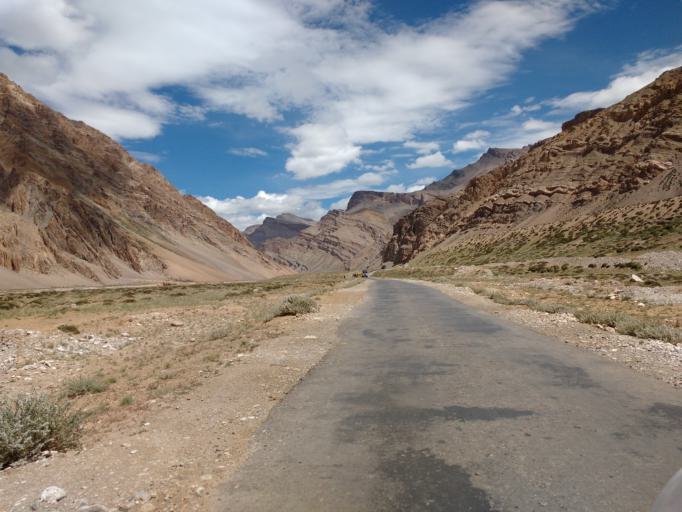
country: IN
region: Himachal Pradesh
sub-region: Lahul and Spiti
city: Kyelang
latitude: 33.0243
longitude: 77.5922
